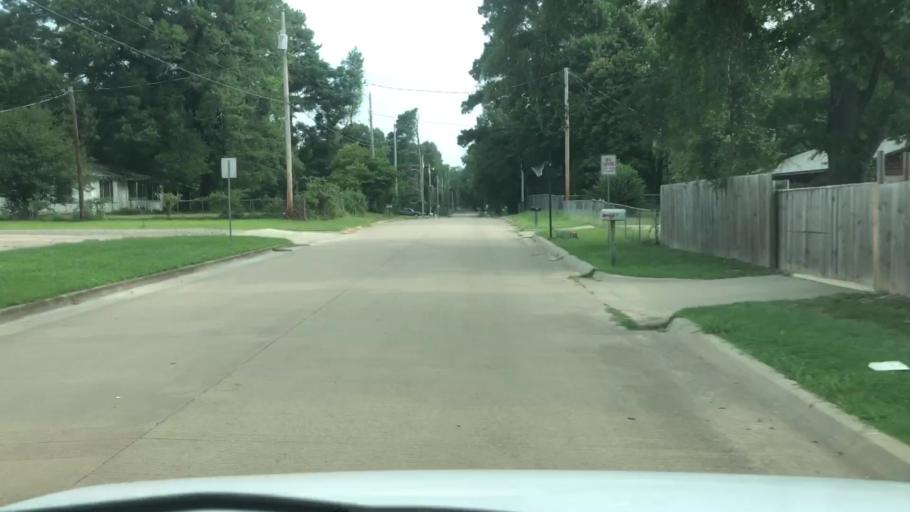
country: US
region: Texas
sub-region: Bowie County
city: Wake Village
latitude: 33.3911
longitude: -94.0856
